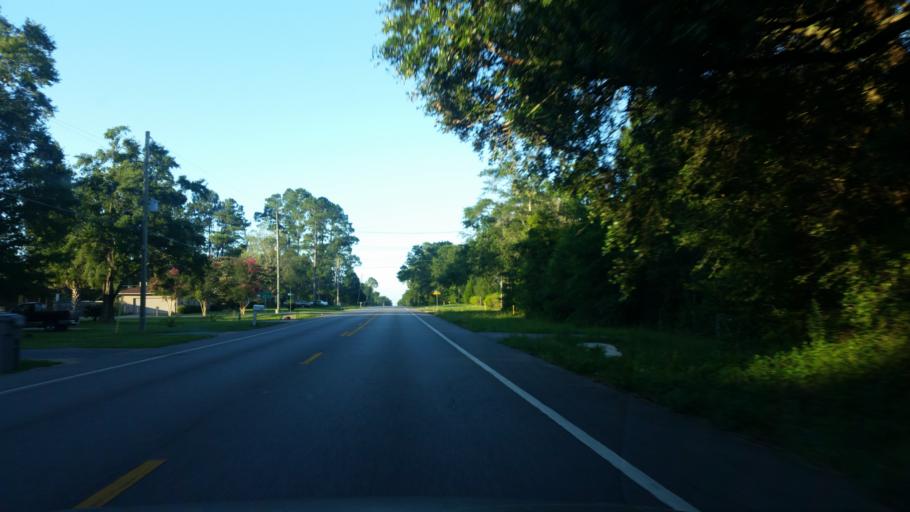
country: US
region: Florida
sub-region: Escambia County
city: Cantonment
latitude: 30.5912
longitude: -87.3492
